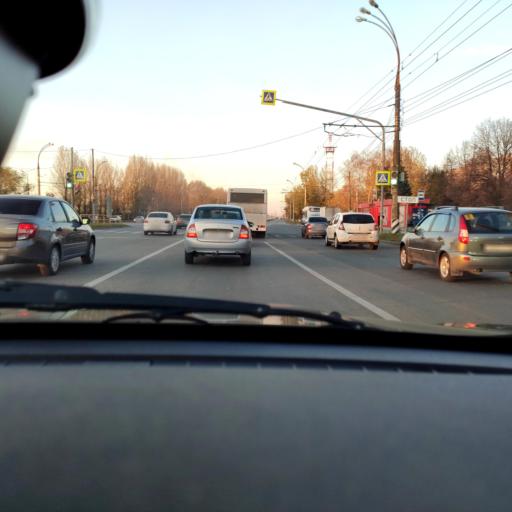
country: RU
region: Samara
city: Tol'yatti
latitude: 53.5241
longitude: 49.2602
